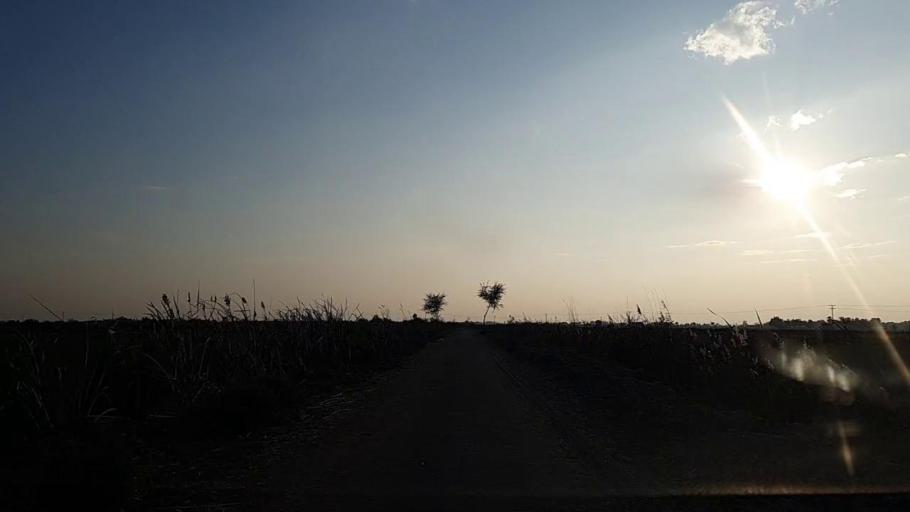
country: PK
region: Sindh
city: Sanghar
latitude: 26.2614
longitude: 68.9784
